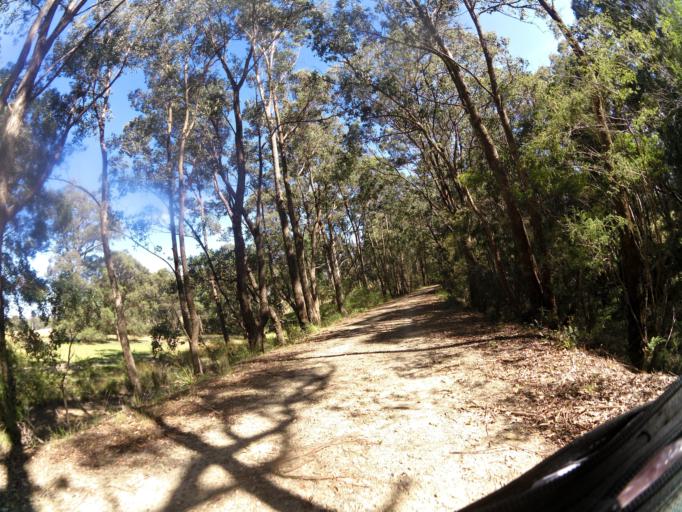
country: AU
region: Victoria
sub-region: East Gippsland
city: Lakes Entrance
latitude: -37.7410
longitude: 148.1693
